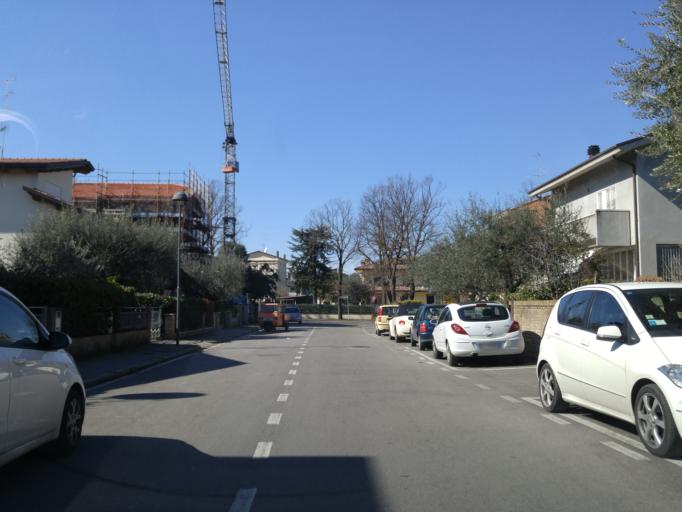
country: IT
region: Emilia-Romagna
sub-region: Provincia di Rimini
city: San Giovanni in Marignano
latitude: 43.9412
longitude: 12.7170
